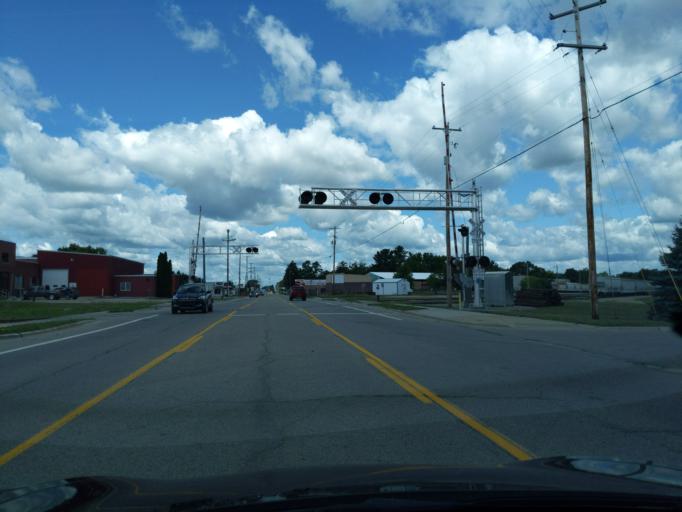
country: US
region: Michigan
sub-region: Clare County
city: Clare
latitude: 43.8198
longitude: -84.7738
